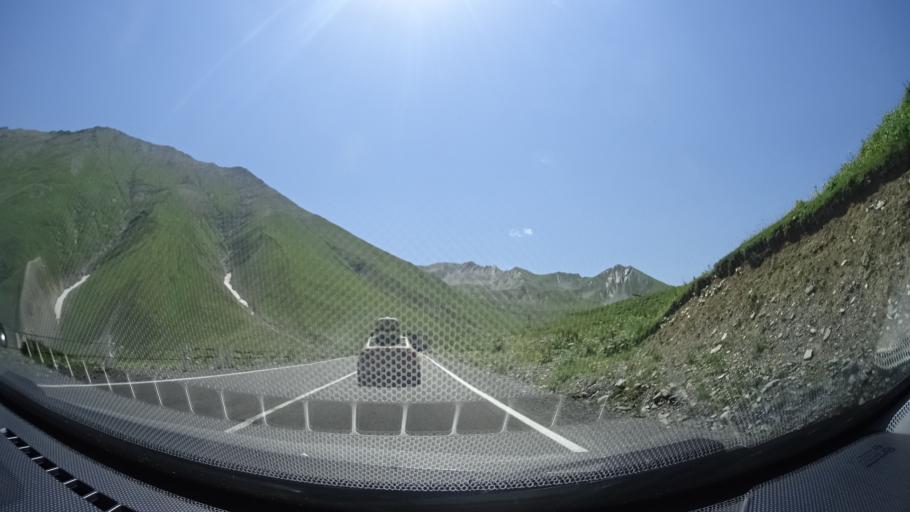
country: GE
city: Gudauri
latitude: 42.5222
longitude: 44.4665
